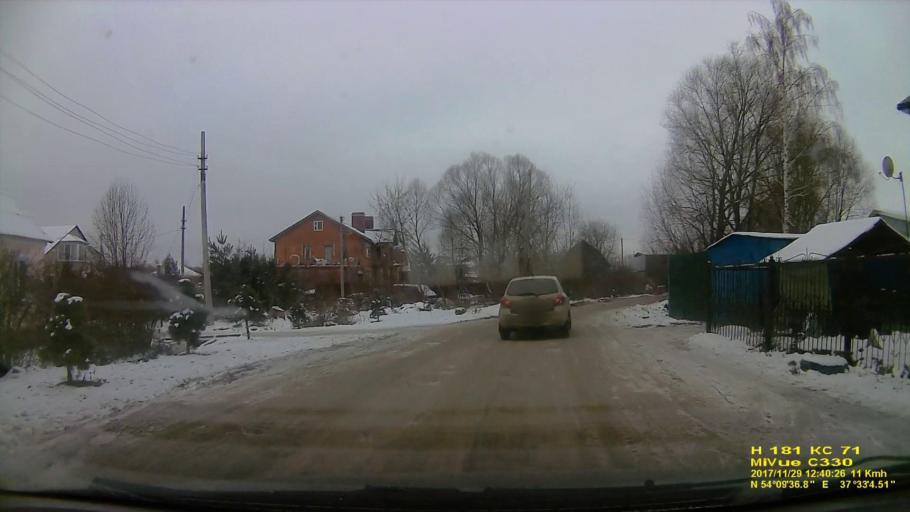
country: RU
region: Tula
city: Kosaya Gora
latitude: 54.1602
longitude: 37.5513
